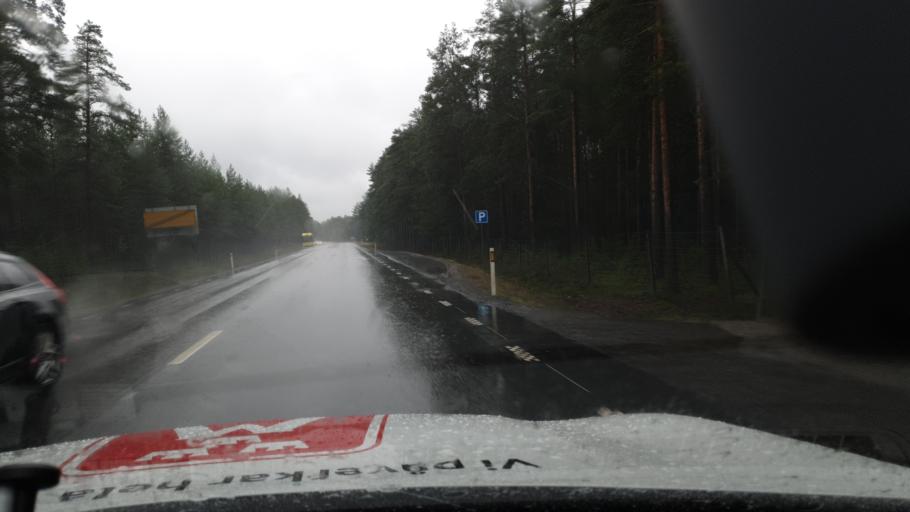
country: SE
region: Vaesterbotten
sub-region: Skelleftea Kommun
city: Burea
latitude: 64.5982
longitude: 21.2067
